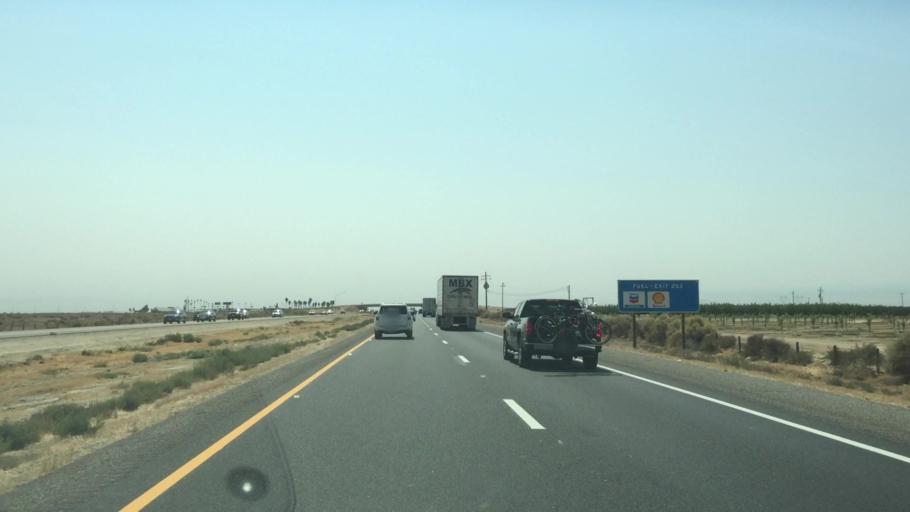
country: US
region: California
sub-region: Kern County
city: Buttonwillow
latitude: 35.3600
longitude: -119.3434
